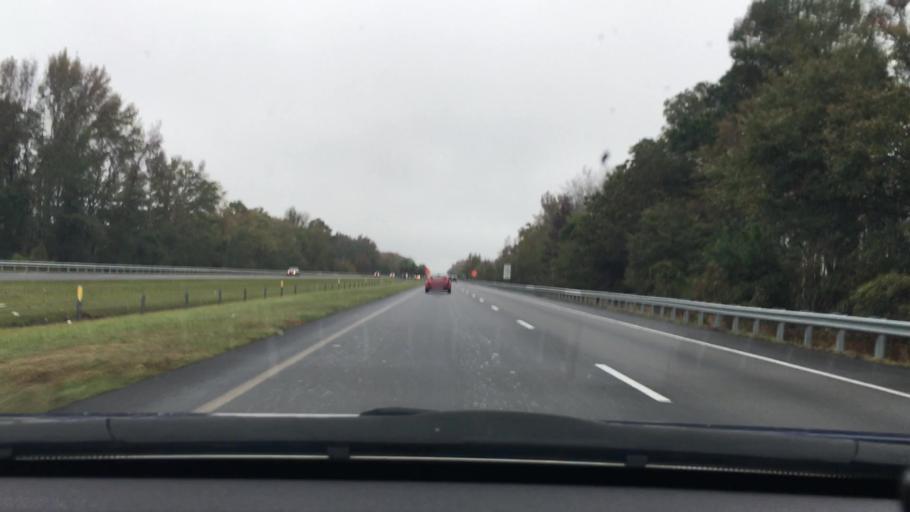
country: US
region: South Carolina
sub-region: Lee County
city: Bishopville
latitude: 34.1888
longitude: -80.1782
